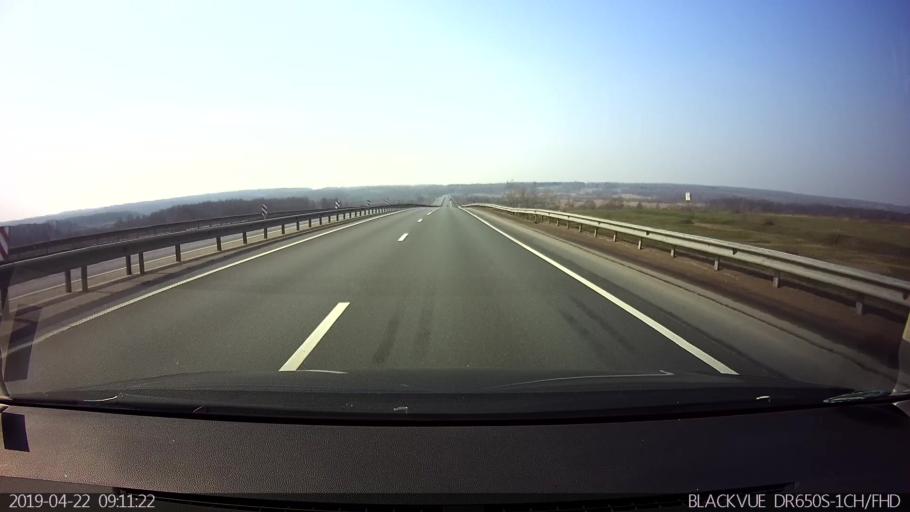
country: RU
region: Smolensk
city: Katyn'
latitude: 54.8267
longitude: 31.6514
